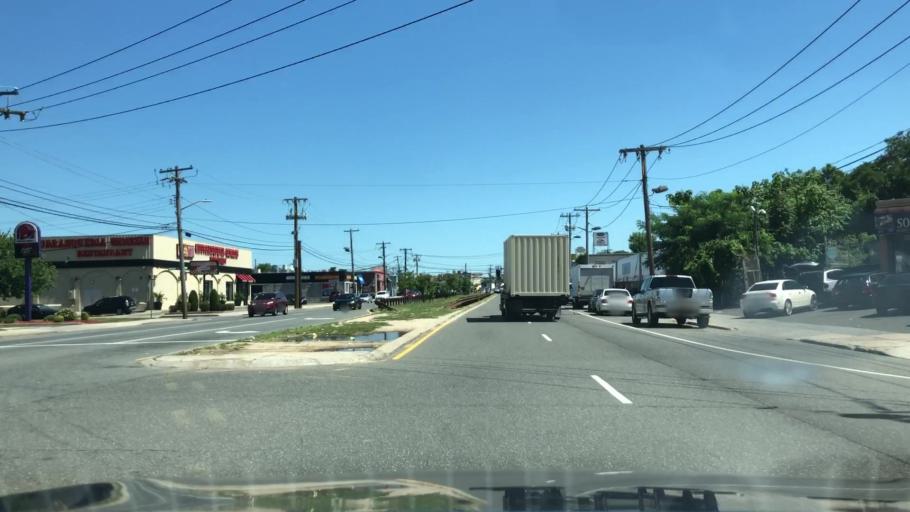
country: US
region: New York
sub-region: Nassau County
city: Hempstead
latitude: 40.7001
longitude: -73.6280
